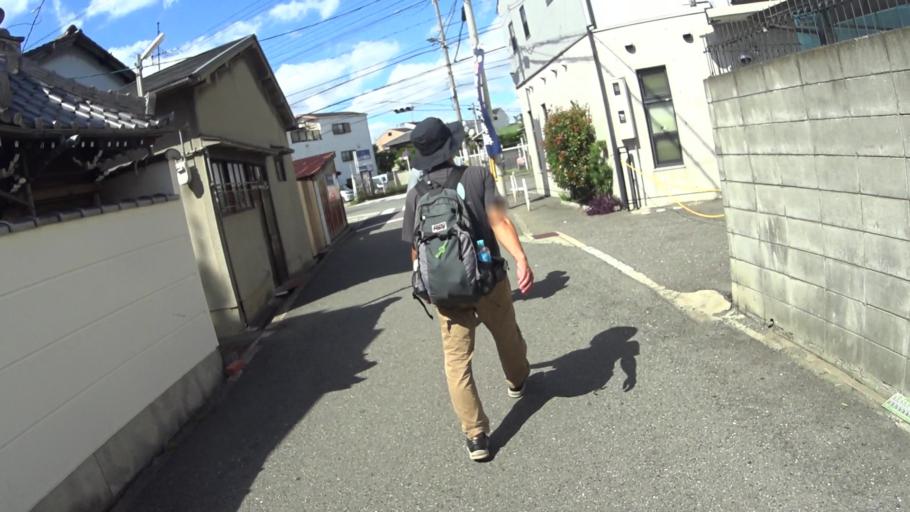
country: JP
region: Osaka
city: Yao
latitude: 34.6423
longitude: 135.5466
